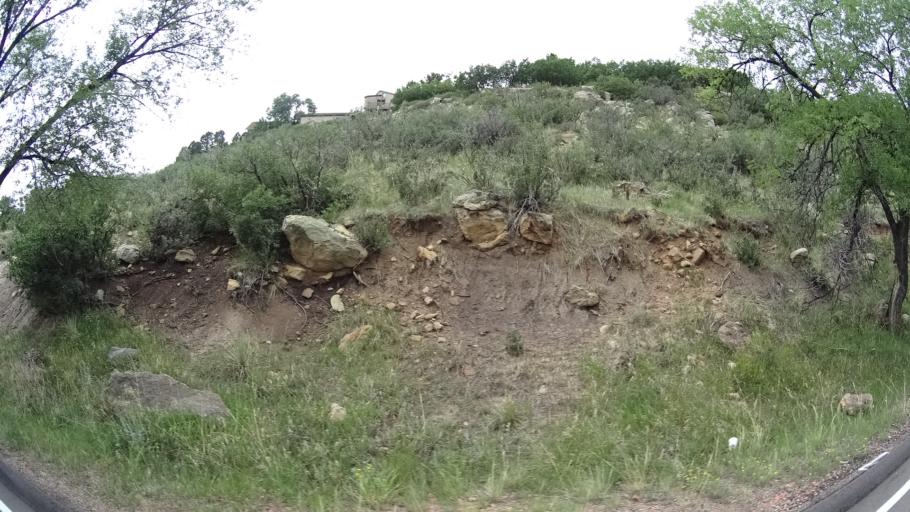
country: US
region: Colorado
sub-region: El Paso County
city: Colorado Springs
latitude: 38.9035
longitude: -104.8314
